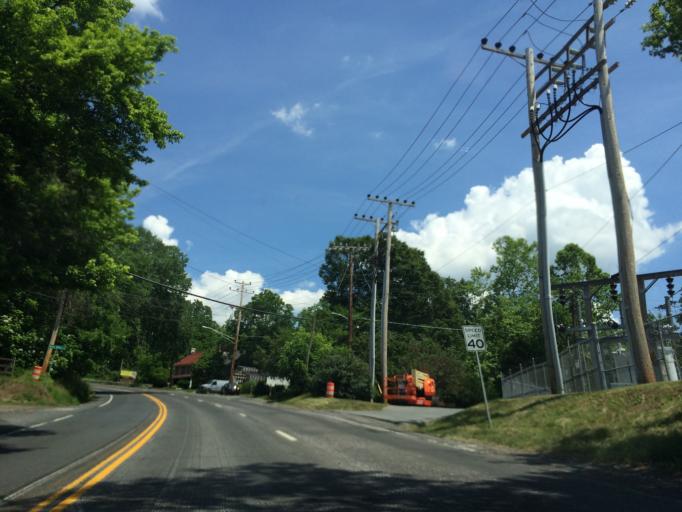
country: US
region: Maryland
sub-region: Howard County
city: Ellicott City
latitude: 39.2624
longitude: -76.7836
